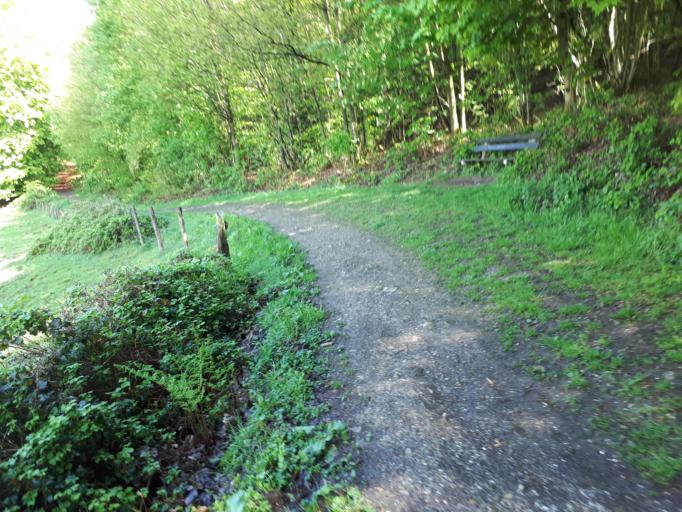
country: NL
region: Limburg
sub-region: Gemeente Vaals
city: Vaals
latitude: 50.7554
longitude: 6.0082
